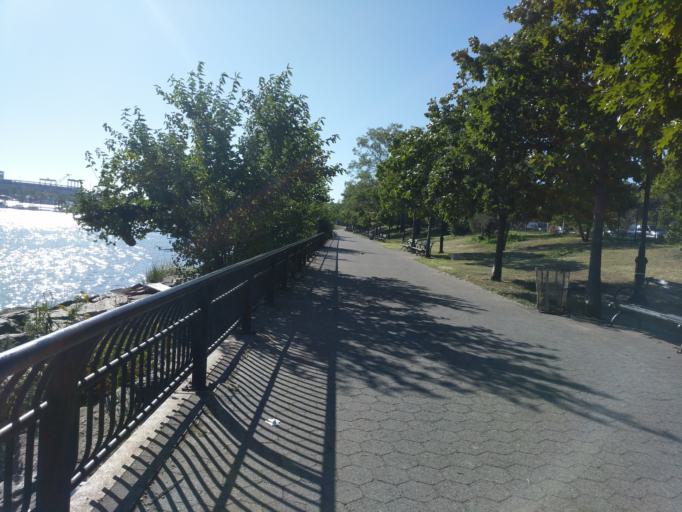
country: US
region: New York
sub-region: Queens County
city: Borough of Queens
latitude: 40.7638
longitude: -73.8606
